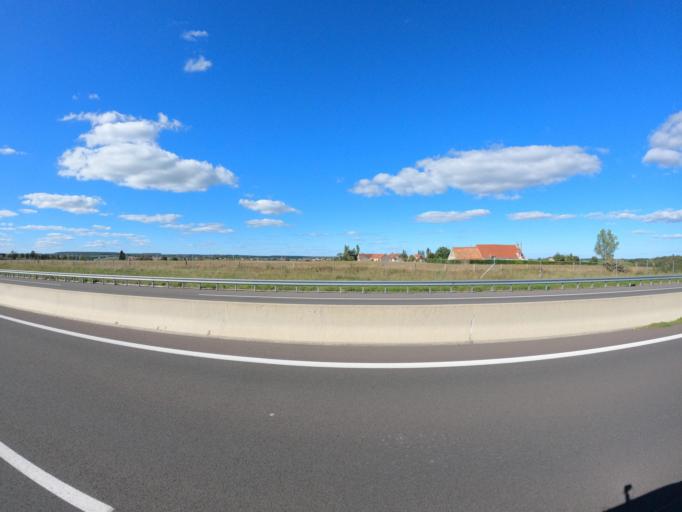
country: FR
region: Auvergne
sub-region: Departement de l'Allier
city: Bessay-sur-Allier
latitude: 46.4579
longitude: 3.2681
